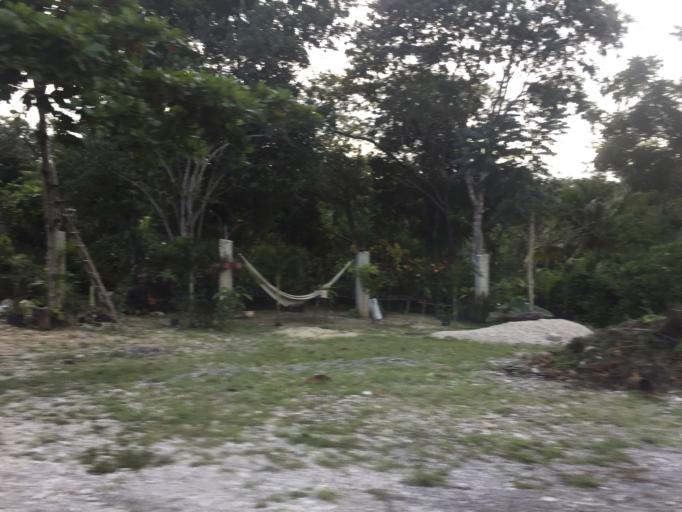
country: MX
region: Quintana Roo
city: Tulum
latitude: 20.3031
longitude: -87.5262
